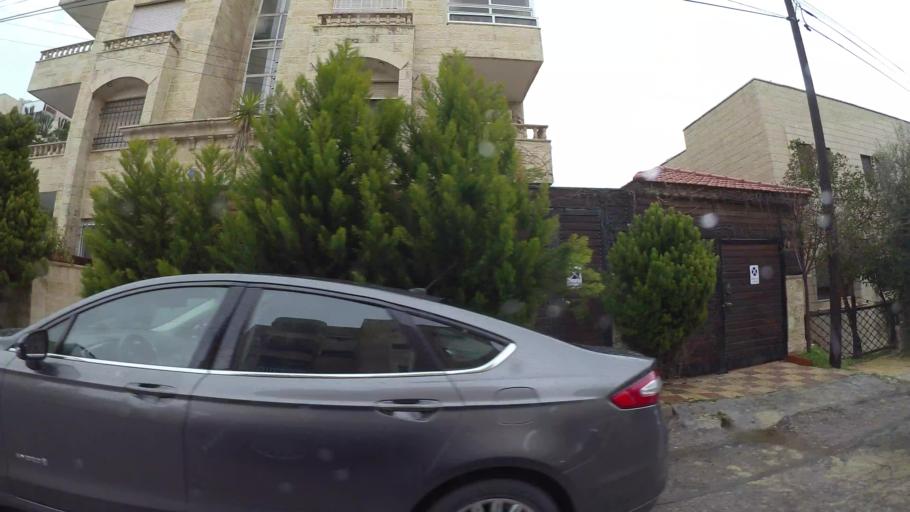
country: JO
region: Amman
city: Wadi as Sir
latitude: 31.9646
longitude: 35.8496
